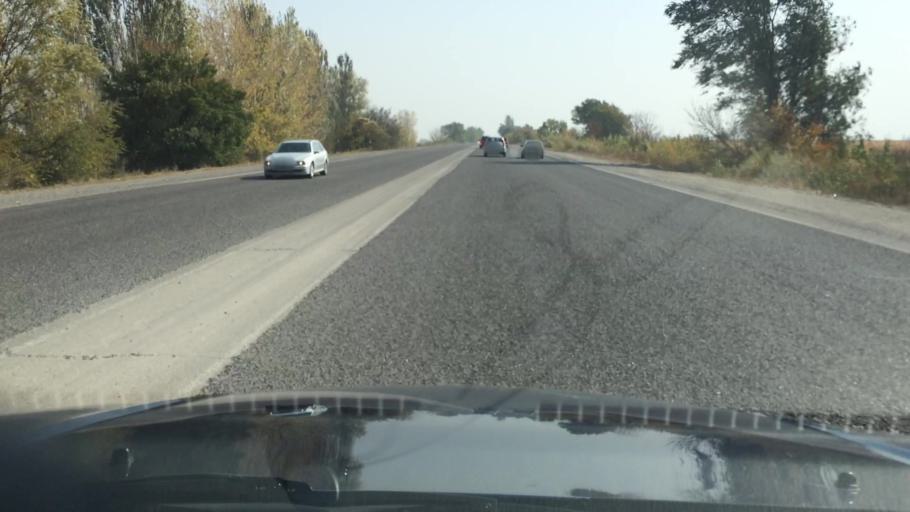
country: KG
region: Chuy
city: Kant
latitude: 42.9565
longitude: 74.9335
